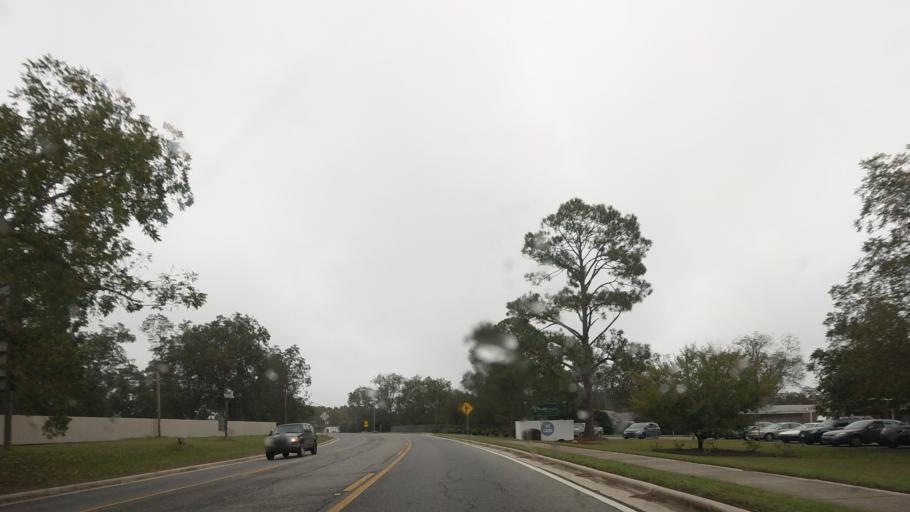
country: US
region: Georgia
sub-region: Ben Hill County
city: Fitzgerald
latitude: 31.7287
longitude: -83.2473
